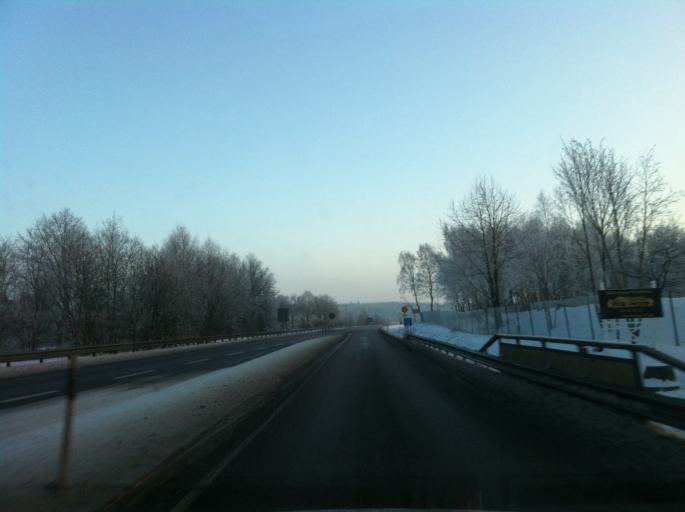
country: SE
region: Skane
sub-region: Bjuvs Kommun
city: Billesholm
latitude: 56.0387
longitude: 13.0197
